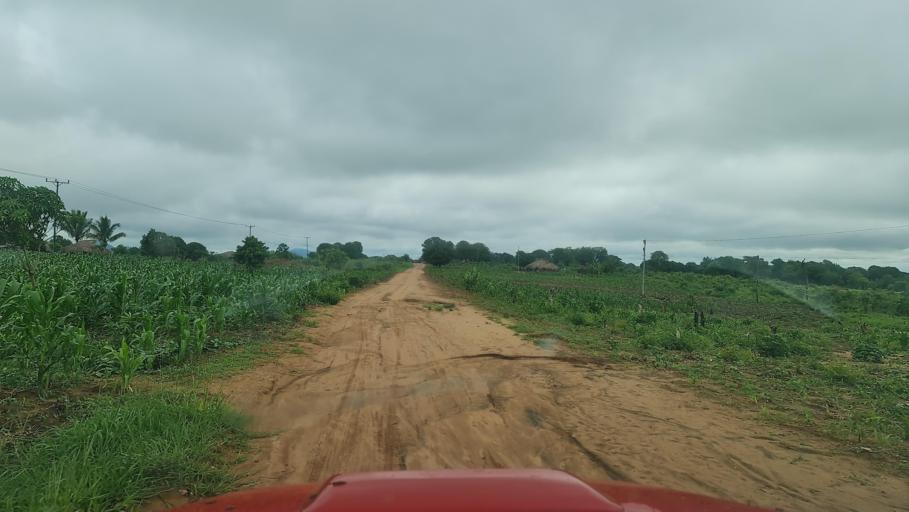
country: MW
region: Southern Region
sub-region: Nsanje District
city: Nsanje
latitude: -17.1976
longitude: 35.8427
